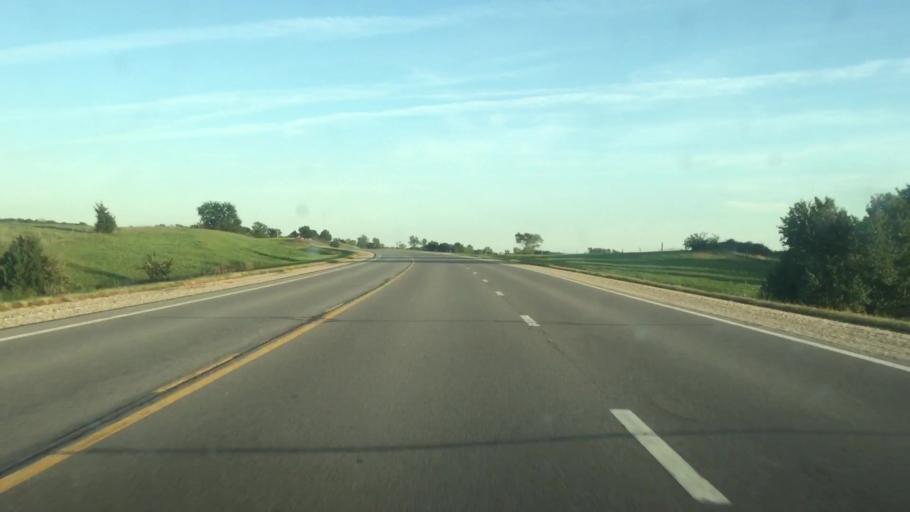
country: US
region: Kansas
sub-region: Atchison County
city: Atchison
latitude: 39.4749
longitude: -95.1025
